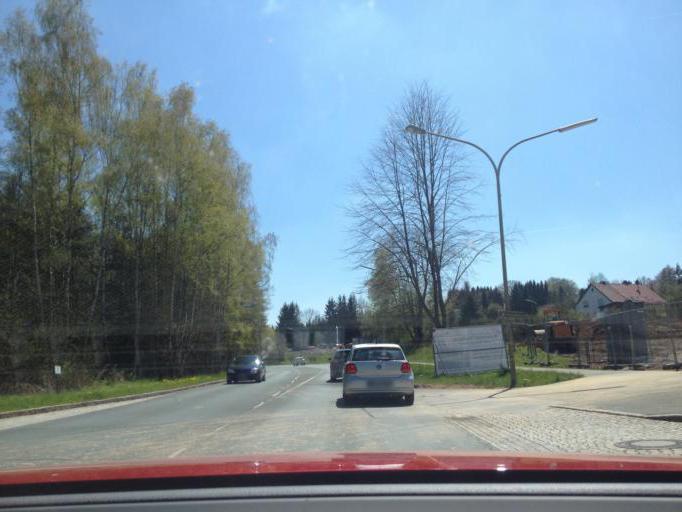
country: DE
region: Bavaria
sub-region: Upper Franconia
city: Oberkotzau
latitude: 50.2567
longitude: 11.9343
